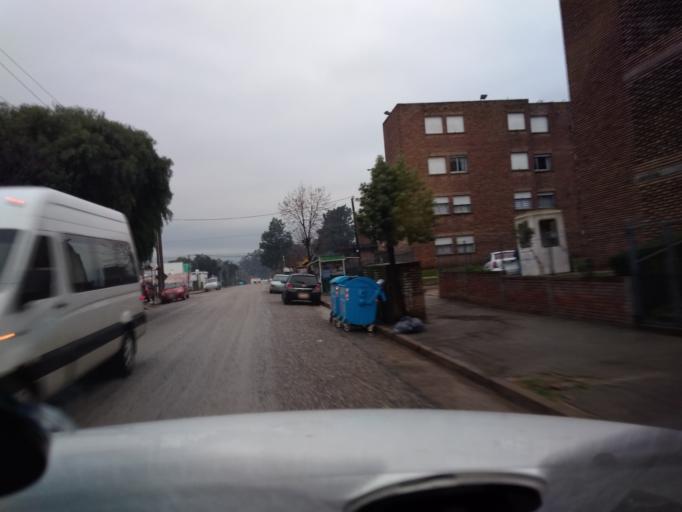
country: UY
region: Florida
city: Florida
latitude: -34.1075
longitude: -56.2098
